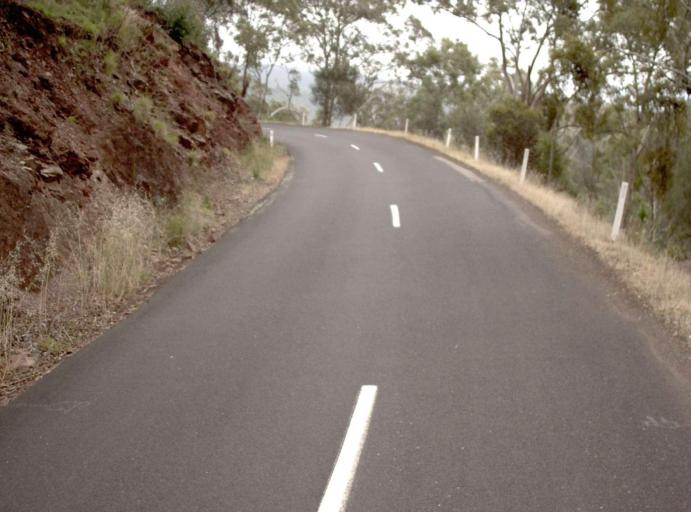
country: AU
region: Victoria
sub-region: Wellington
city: Heyfield
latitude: -37.7045
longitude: 146.6670
